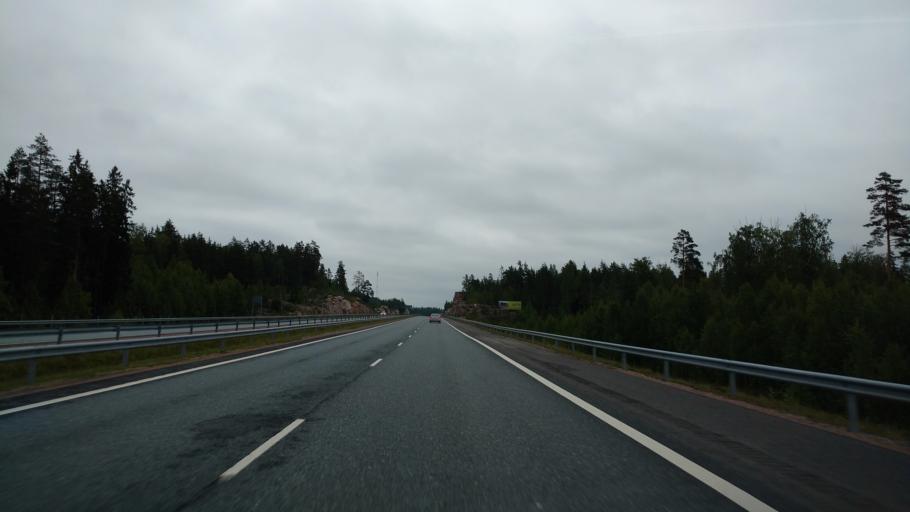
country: FI
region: Varsinais-Suomi
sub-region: Salo
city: Muurla
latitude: 60.3752
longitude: 23.4018
